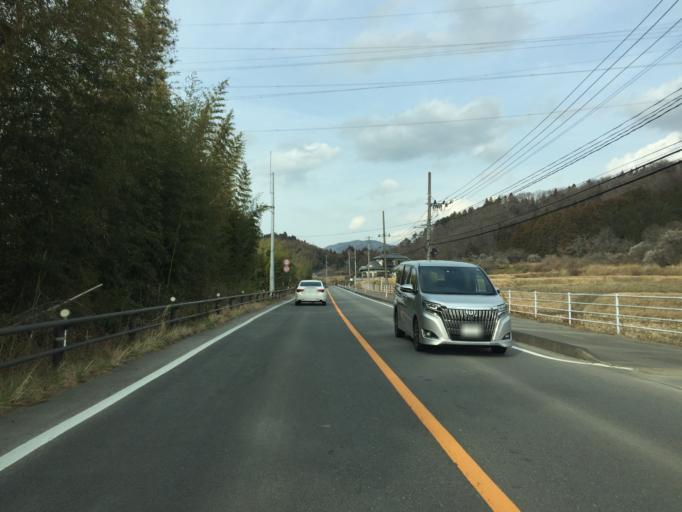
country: JP
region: Fukushima
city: Iwaki
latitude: 36.9852
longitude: 140.7368
